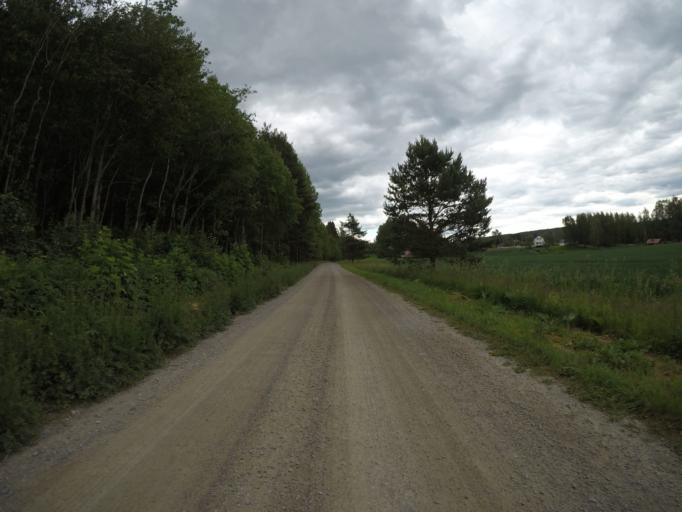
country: FI
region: Haeme
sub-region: Haemeenlinna
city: Haemeenlinna
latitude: 60.9762
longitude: 24.4567
